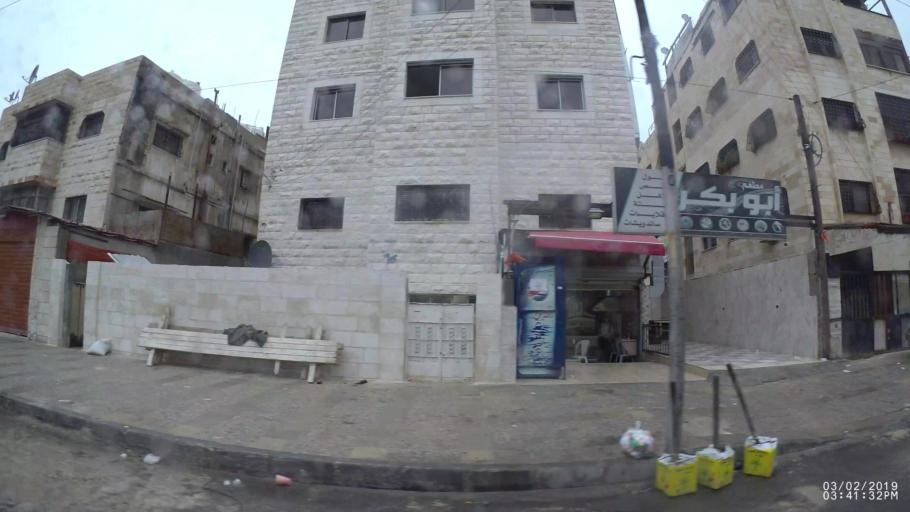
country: JO
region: Amman
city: Amman
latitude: 31.9743
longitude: 35.9198
